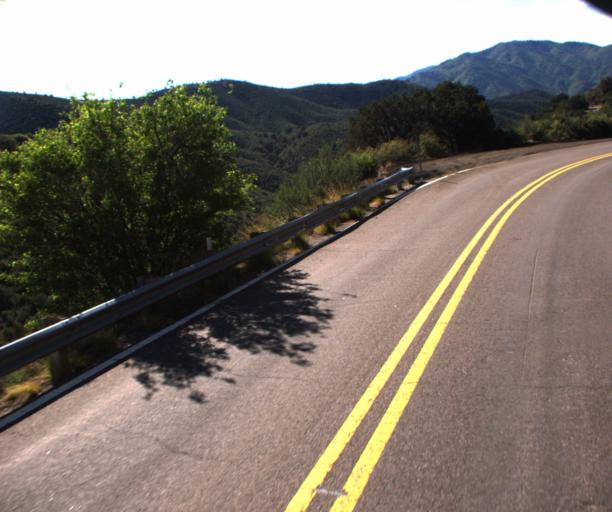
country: US
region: Arizona
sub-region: Yavapai County
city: Prescott
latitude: 34.4653
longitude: -112.5200
